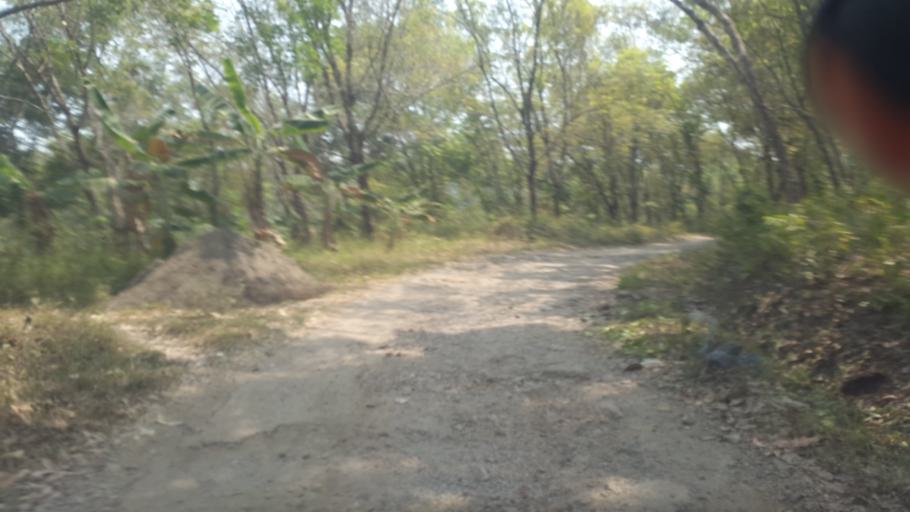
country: ID
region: West Java
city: Cimaja
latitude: -6.9390
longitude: 106.4991
